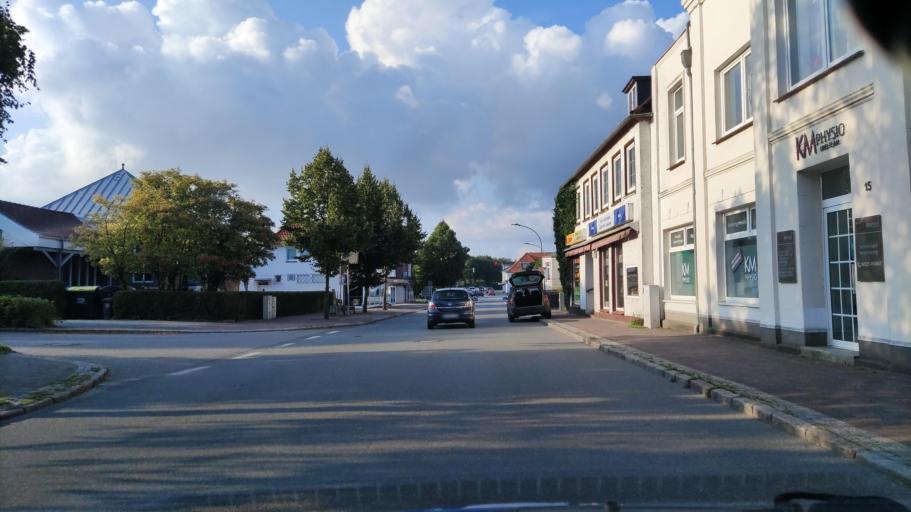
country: DE
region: Schleswig-Holstein
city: Ahrensbok
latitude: 54.0088
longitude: 10.5739
